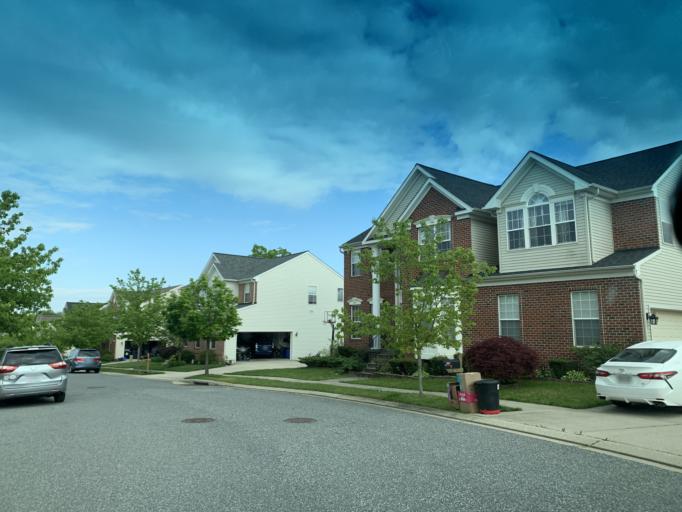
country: US
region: Maryland
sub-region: Baltimore County
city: White Marsh
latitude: 39.4040
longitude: -76.4286
